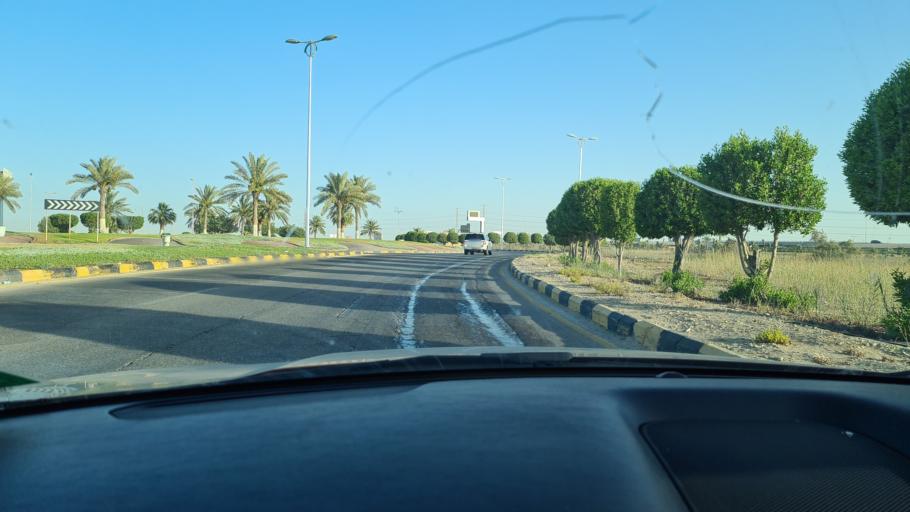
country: SA
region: Eastern Province
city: Al Jubayl
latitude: 26.9279
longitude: 49.7110
